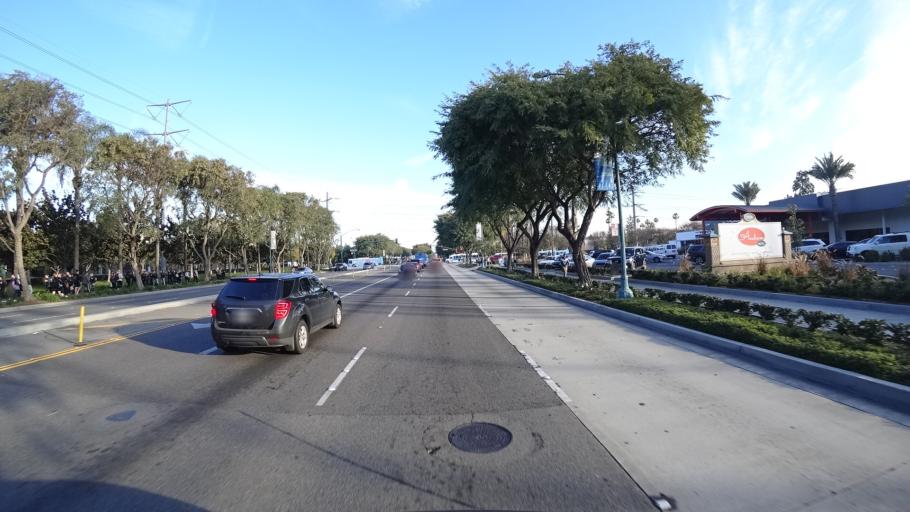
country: US
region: California
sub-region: Orange County
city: Anaheim
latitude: 33.8058
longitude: -117.9151
